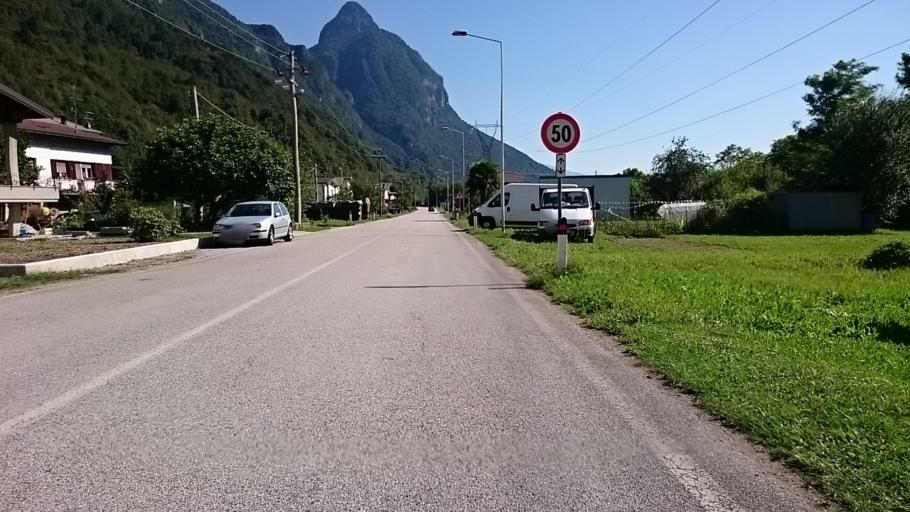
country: IT
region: Veneto
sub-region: Provincia di Belluno
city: Longarone
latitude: 46.2606
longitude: 12.3127
